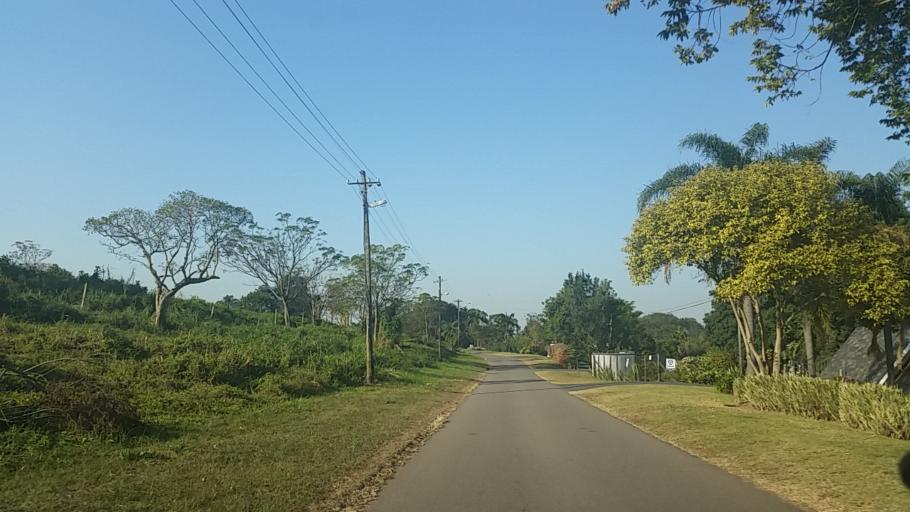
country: ZA
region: KwaZulu-Natal
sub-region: eThekwini Metropolitan Municipality
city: Berea
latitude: -29.8506
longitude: 30.9085
